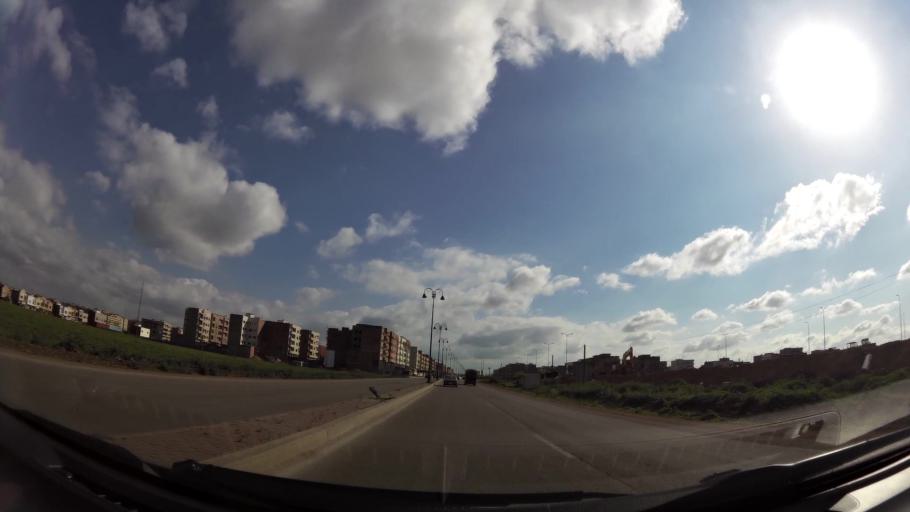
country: MA
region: Chaouia-Ouardigha
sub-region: Settat Province
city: Berrechid
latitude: 33.2803
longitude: -7.5804
